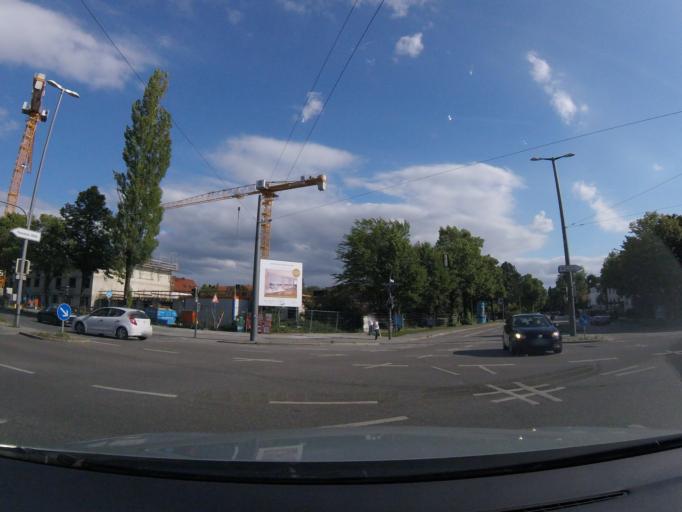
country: DE
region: Bavaria
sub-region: Upper Bavaria
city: Bogenhausen
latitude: 48.1536
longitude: 11.6295
